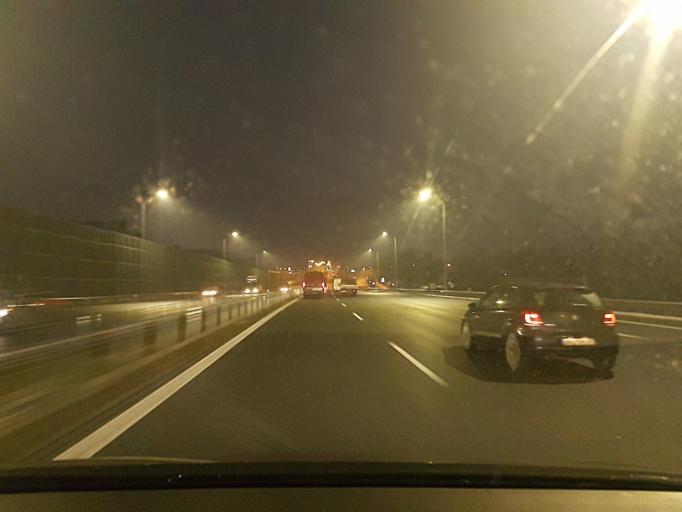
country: PL
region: Masovian Voivodeship
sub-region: Powiat wolominski
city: Marki
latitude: 52.3074
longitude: 21.1018
